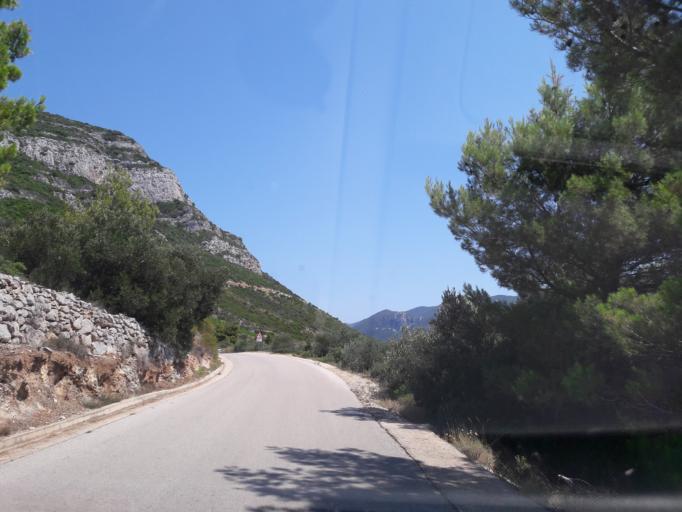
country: HR
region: Dubrovacko-Neretvanska
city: Blato
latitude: 42.9036
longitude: 17.4280
